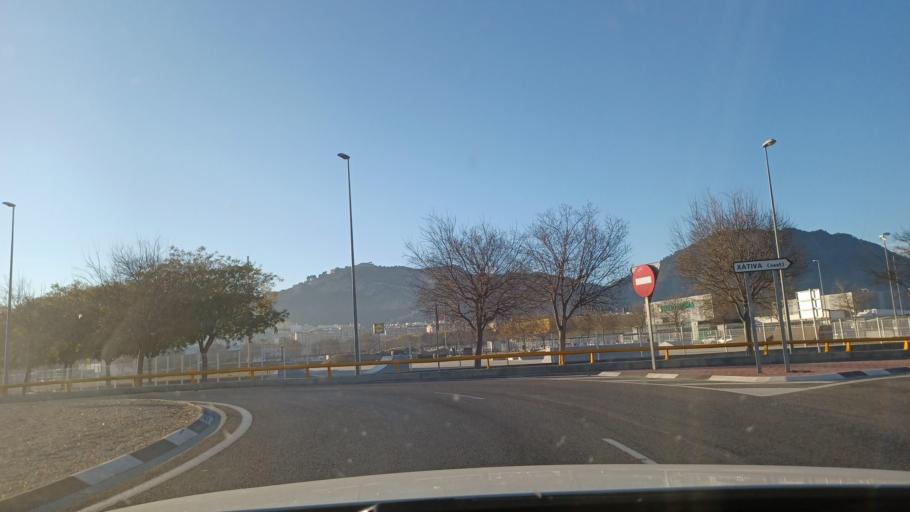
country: ES
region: Valencia
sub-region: Provincia de Valencia
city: Xativa
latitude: 38.9991
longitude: -0.5263
